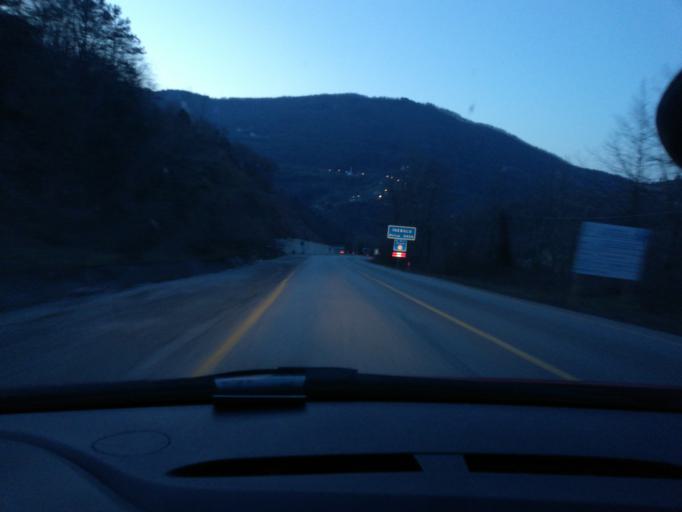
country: TR
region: Kastamonu
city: Inebolu
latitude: 41.9510
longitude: 33.7554
